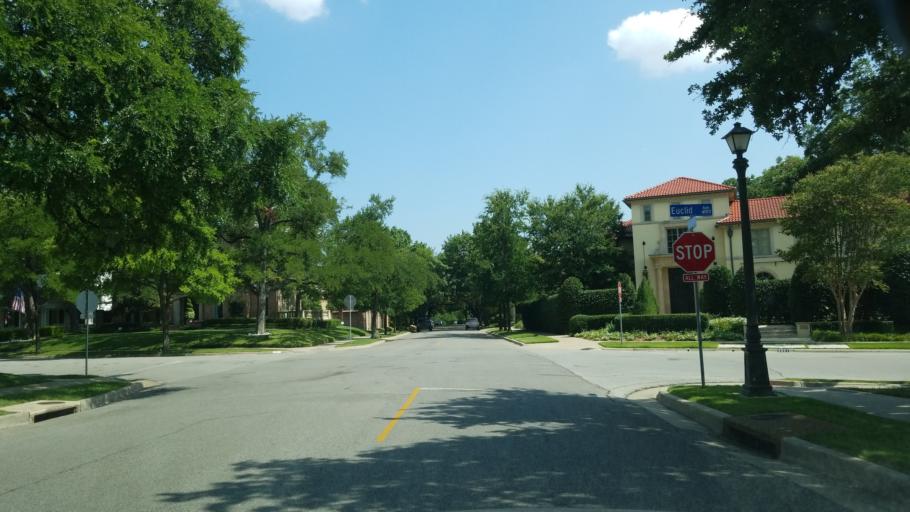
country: US
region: Texas
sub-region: Dallas County
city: Highland Park
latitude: 32.8282
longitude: -96.8000
